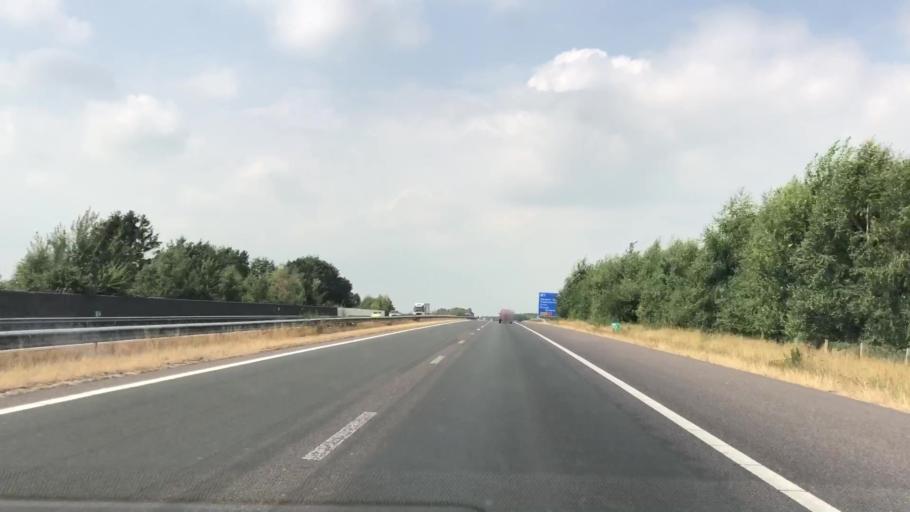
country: NL
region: Drenthe
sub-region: Gemeente Emmen
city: Klazienaveen
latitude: 52.7345
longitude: 6.9888
